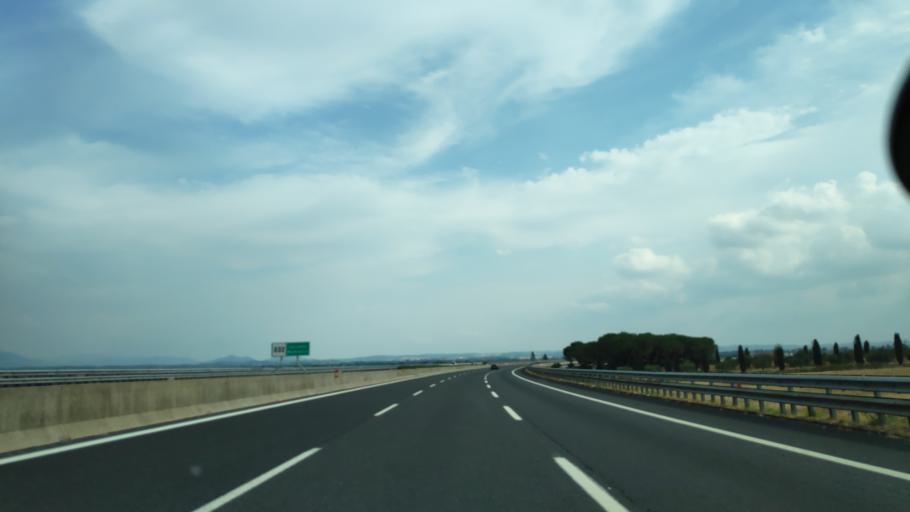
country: IT
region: Latium
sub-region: Citta metropolitana di Roma Capitale
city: Fiano Romano
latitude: 42.1554
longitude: 12.6241
